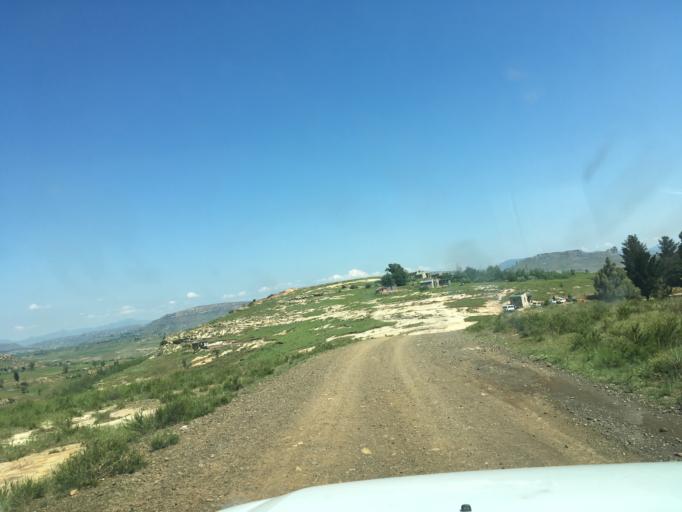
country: LS
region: Butha-Buthe
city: Butha-Buthe
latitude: -28.7267
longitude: 28.3606
